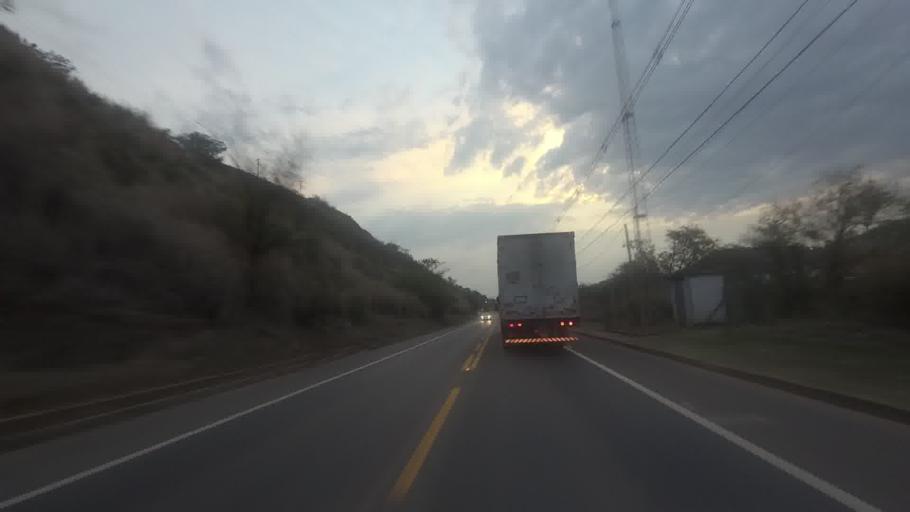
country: BR
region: Minas Gerais
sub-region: Alem Paraiba
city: Alem Paraiba
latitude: -21.8856
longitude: -42.6943
